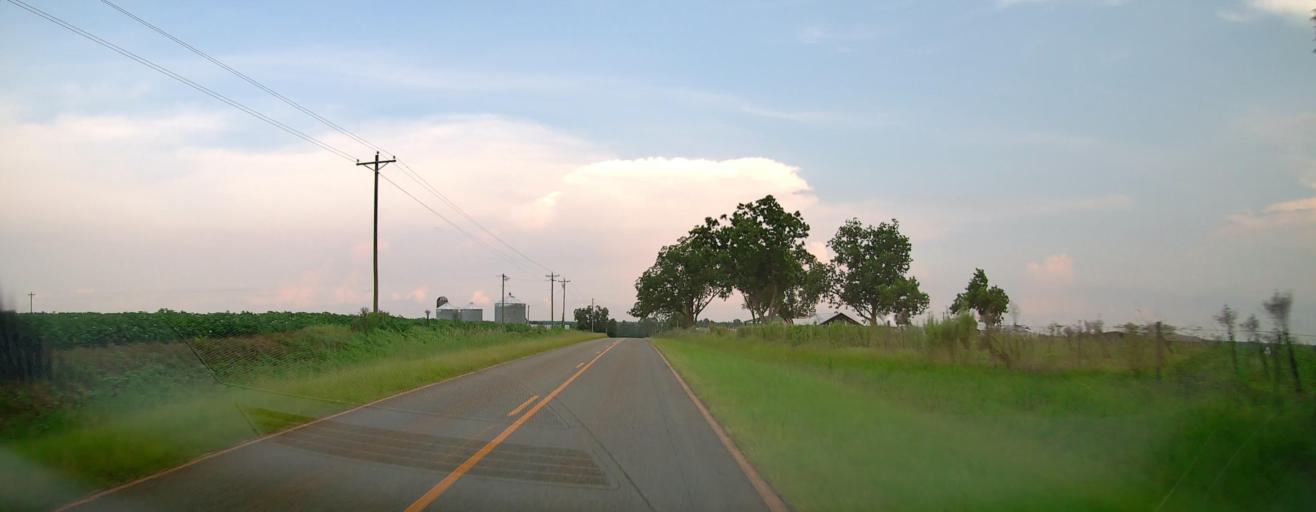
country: US
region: Georgia
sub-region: Laurens County
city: East Dublin
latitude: 32.6439
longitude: -82.8171
